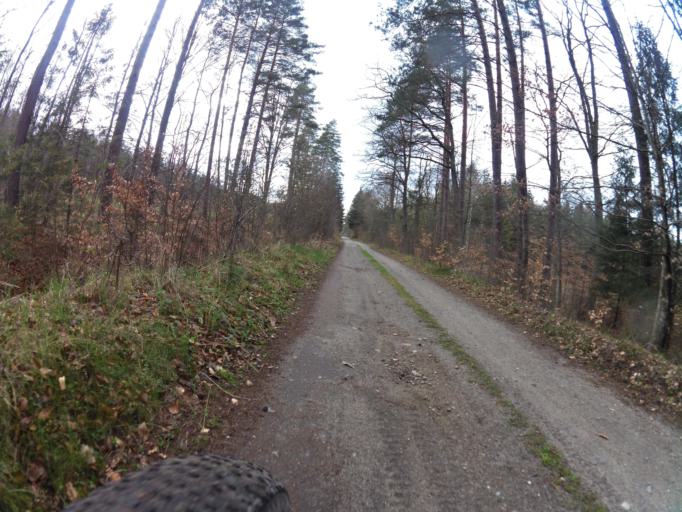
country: PL
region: West Pomeranian Voivodeship
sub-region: Powiat slawienski
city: Slawno
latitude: 54.3203
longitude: 16.7766
